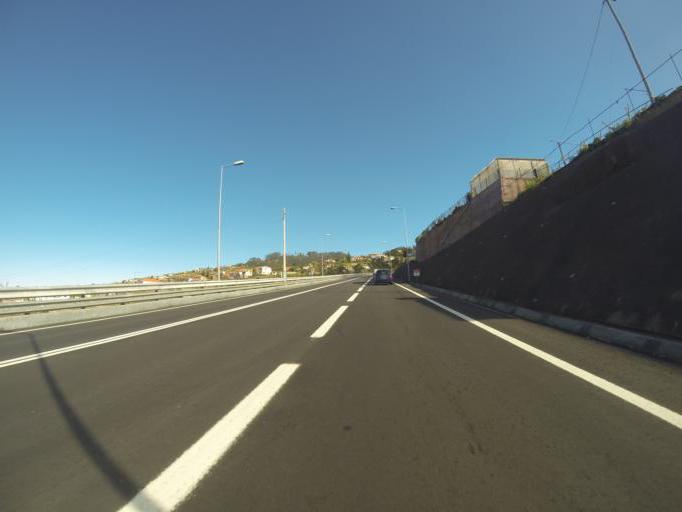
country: PT
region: Madeira
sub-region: Calheta
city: Estreito da Calheta
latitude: 32.7402
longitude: -17.1945
